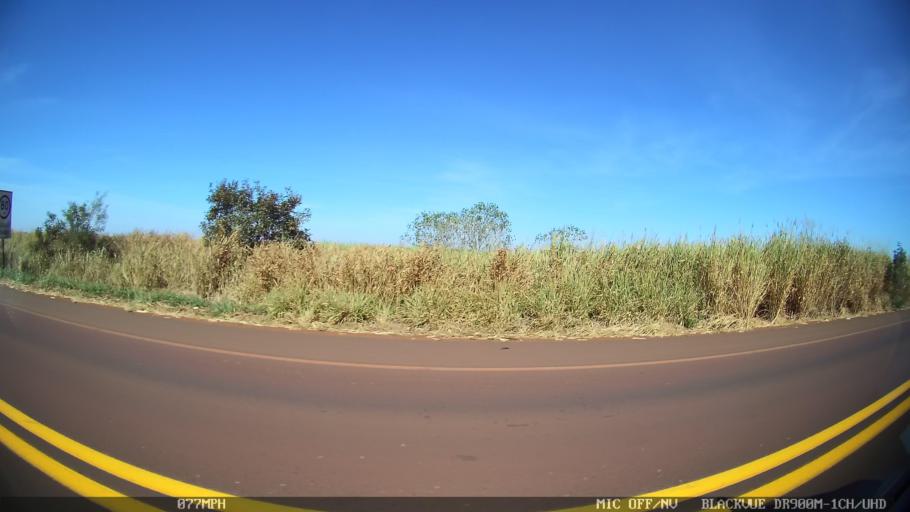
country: BR
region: Sao Paulo
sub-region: Barretos
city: Barretos
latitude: -20.4646
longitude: -48.4739
